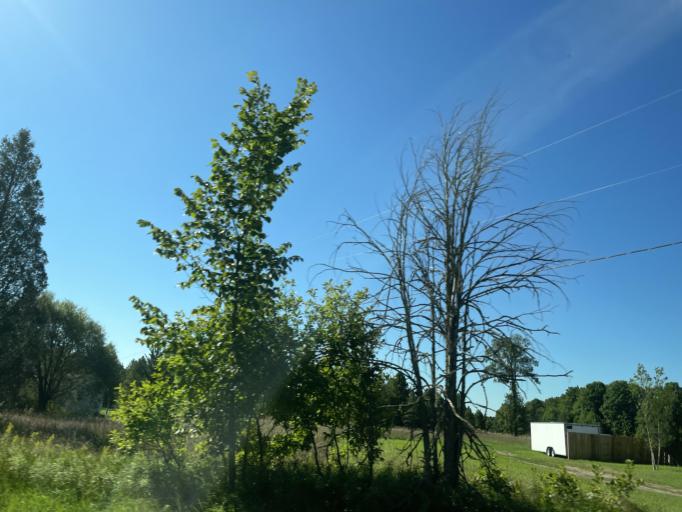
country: US
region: Michigan
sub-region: Benzie County
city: Beulah
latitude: 44.6172
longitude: -86.0411
